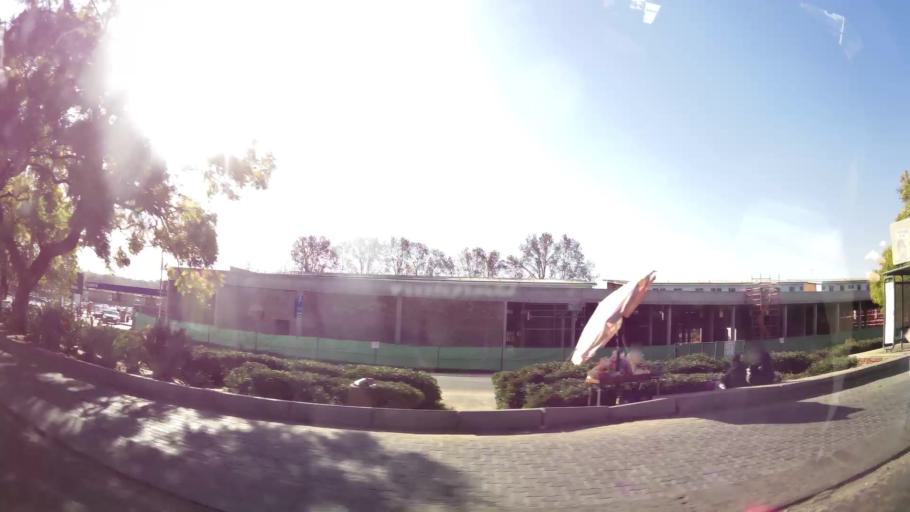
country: ZA
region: Gauteng
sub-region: City of Tshwane Metropolitan Municipality
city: Pretoria
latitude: -25.7328
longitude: 28.2468
